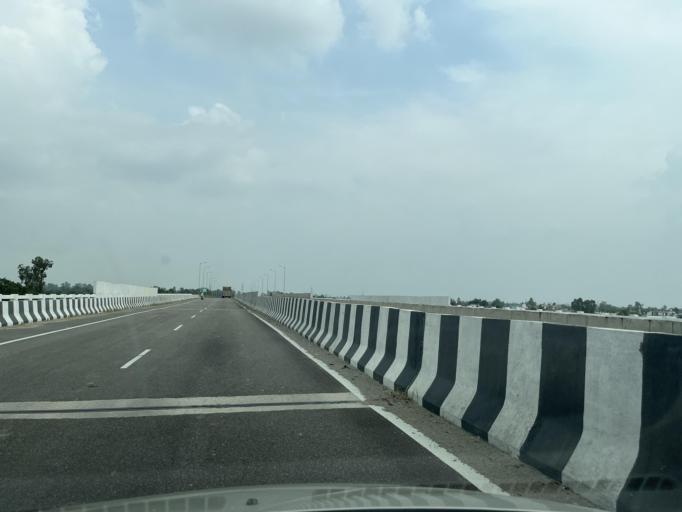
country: IN
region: Uttarakhand
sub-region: Udham Singh Nagar
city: Kashipur
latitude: 29.1737
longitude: 78.9464
